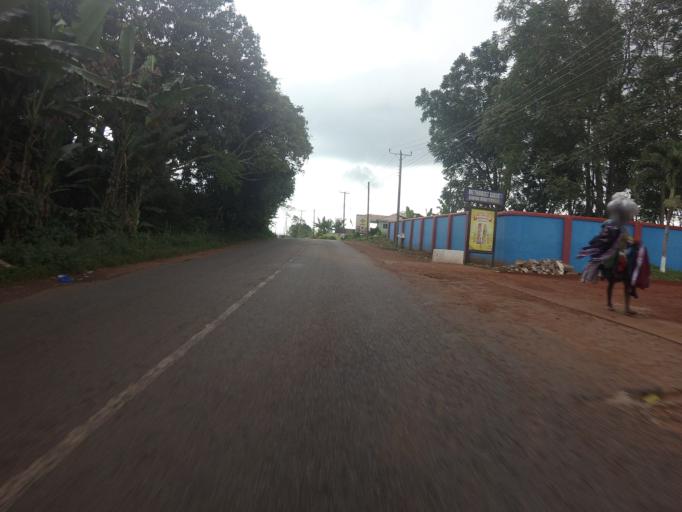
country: GH
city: Akropong
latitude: 5.9419
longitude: -0.1192
